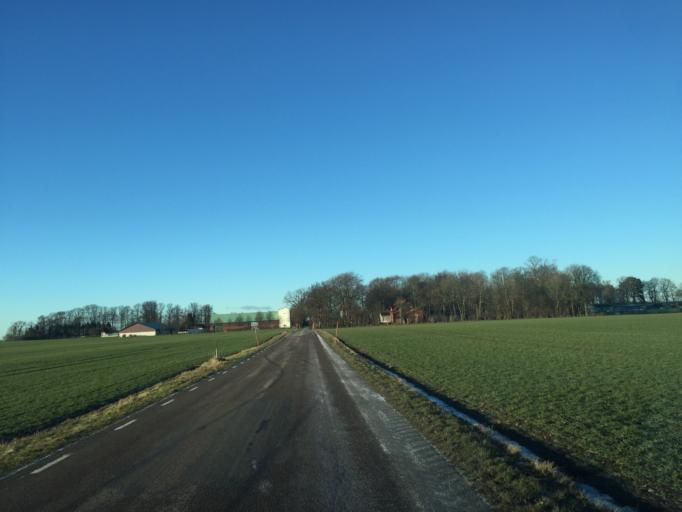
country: SE
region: Skane
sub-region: Kavlinge Kommun
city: Kaevlinge
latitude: 55.7587
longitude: 13.0751
